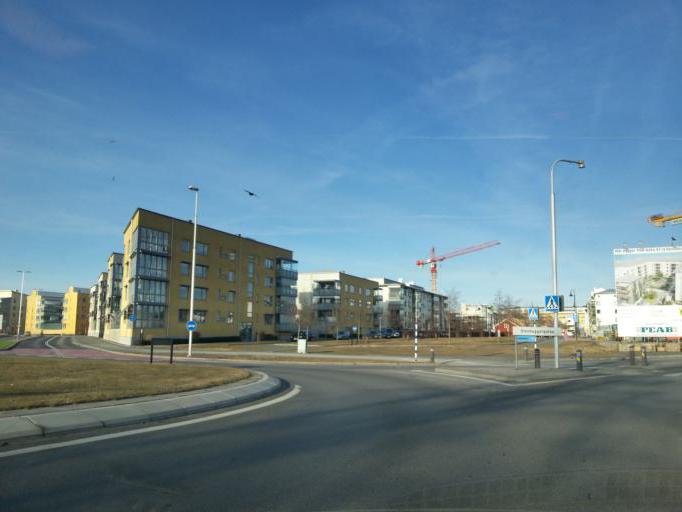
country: SE
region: Joenkoeping
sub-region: Jonkopings Kommun
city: Jonkoping
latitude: 57.7753
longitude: 14.1759
